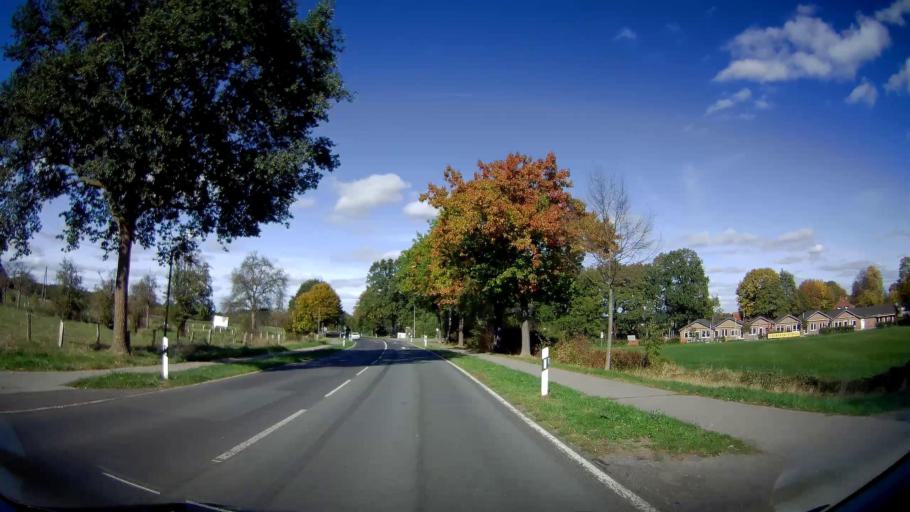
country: DE
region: North Rhine-Westphalia
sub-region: Regierungsbezirk Dusseldorf
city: Hunxe
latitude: 51.6360
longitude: 6.7619
